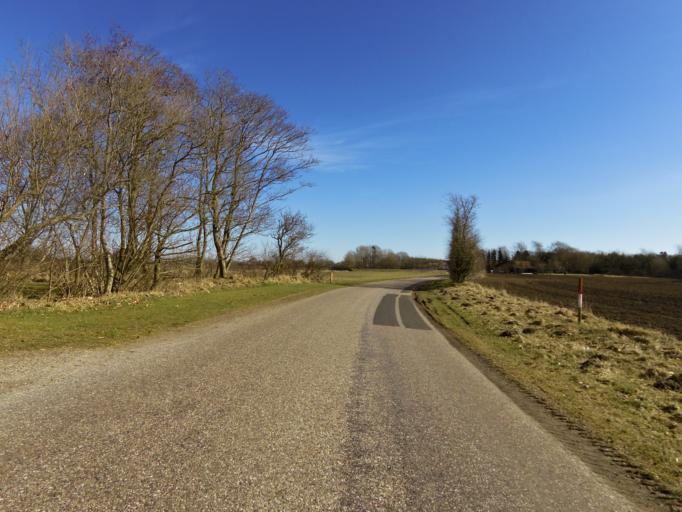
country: DK
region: South Denmark
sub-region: Tonder Kommune
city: Toftlund
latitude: 55.2358
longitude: 9.1194
